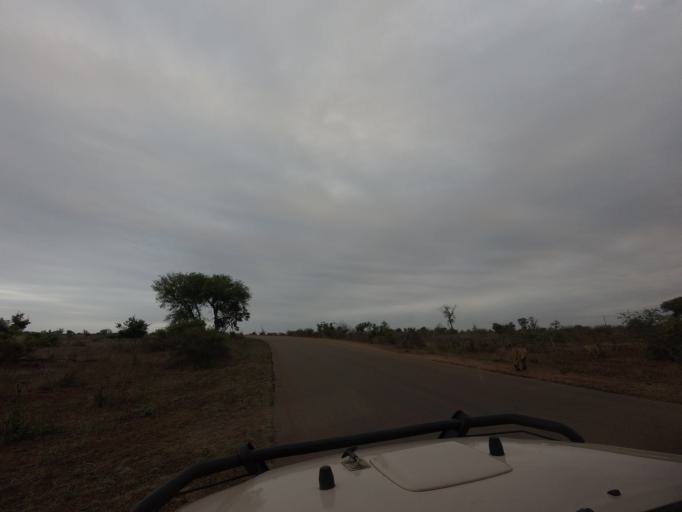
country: ZA
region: Mpumalanga
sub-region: Ehlanzeni District
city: Komatipoort
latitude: -25.3548
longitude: 31.8896
